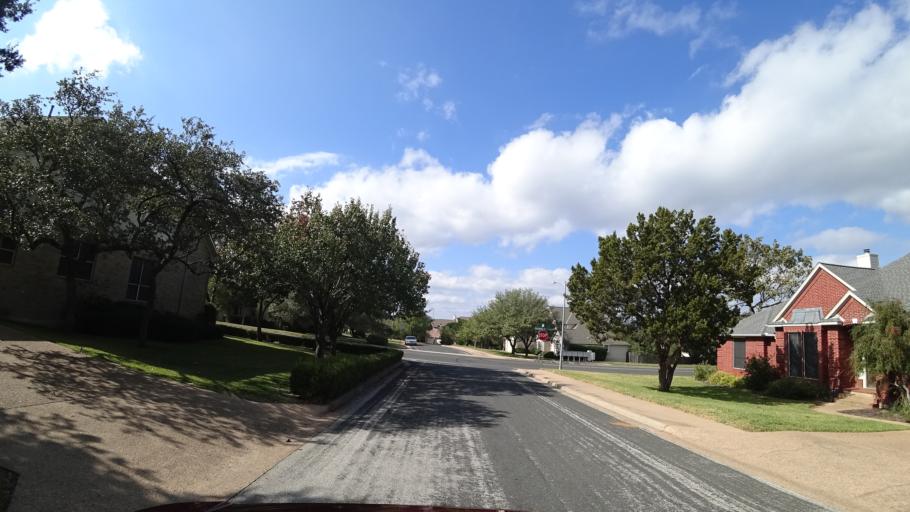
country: US
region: Texas
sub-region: Williamson County
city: Jollyville
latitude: 30.4183
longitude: -97.7914
